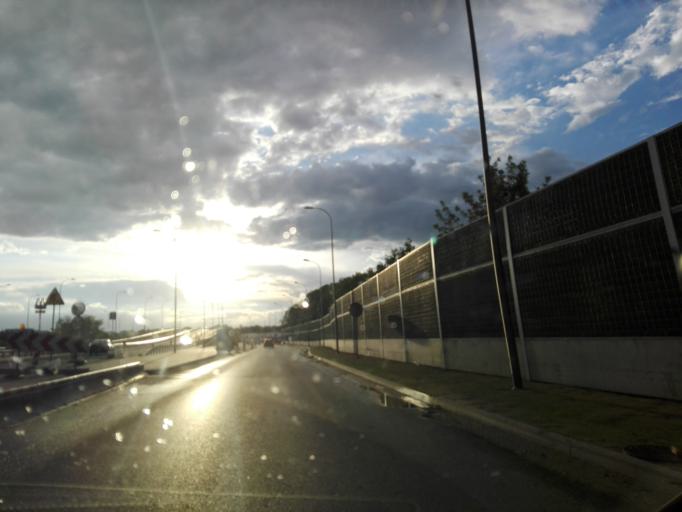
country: PL
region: Lublin Voivodeship
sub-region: Powiat lubelski
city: Lublin
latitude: 51.2574
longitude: 22.5369
